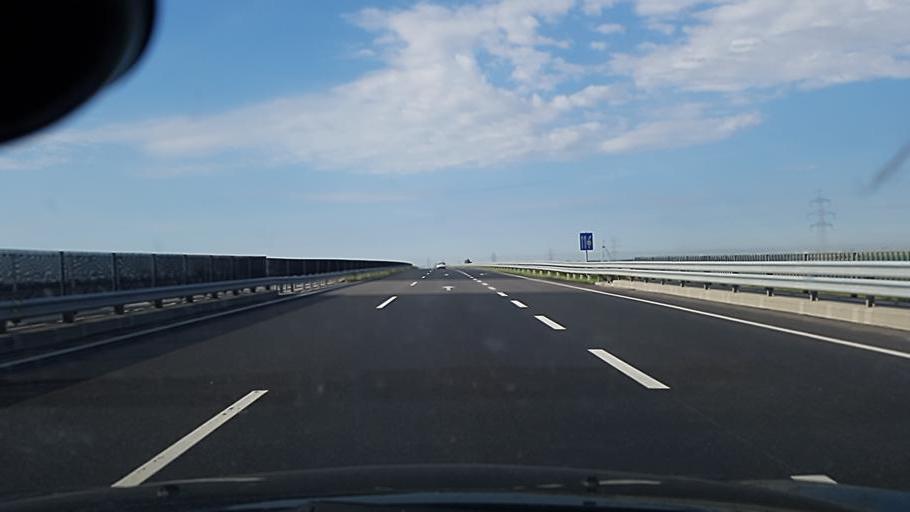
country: HU
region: Fejer
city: Ivancsa
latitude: 47.1781
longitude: 18.8065
